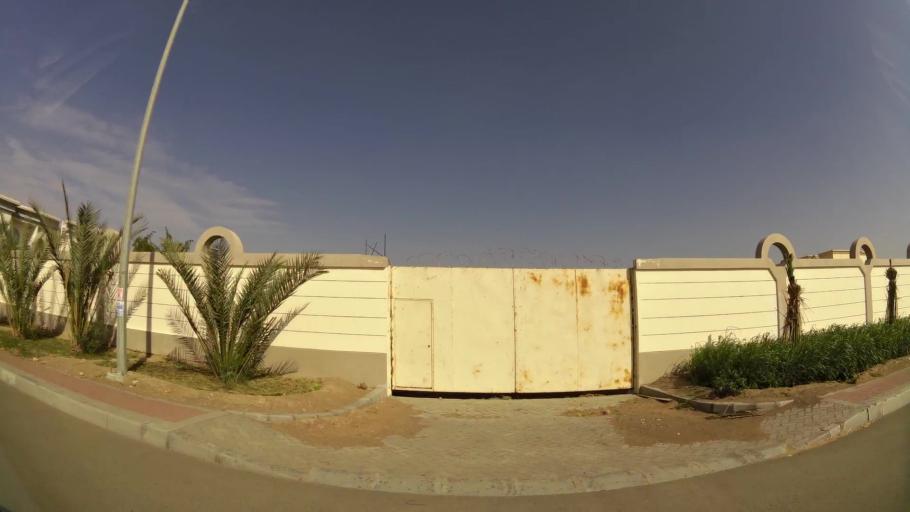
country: AE
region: Abu Dhabi
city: Al Ain
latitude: 24.0916
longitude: 55.9012
